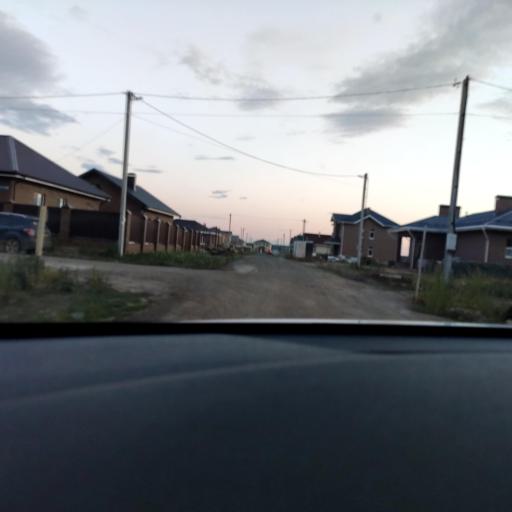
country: RU
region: Tatarstan
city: Stolbishchi
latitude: 55.7200
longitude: 49.2985
